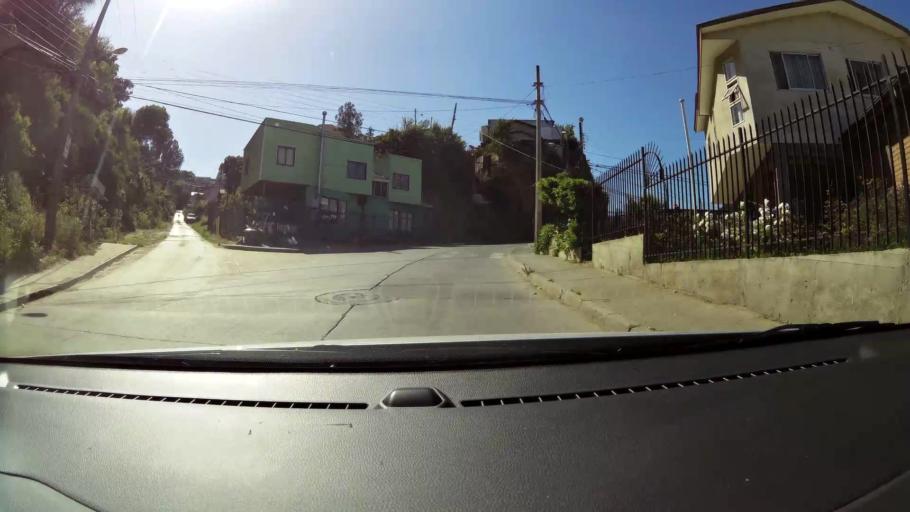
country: CL
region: Valparaiso
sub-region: Provincia de Valparaiso
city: Valparaiso
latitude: -33.0622
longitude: -71.5902
